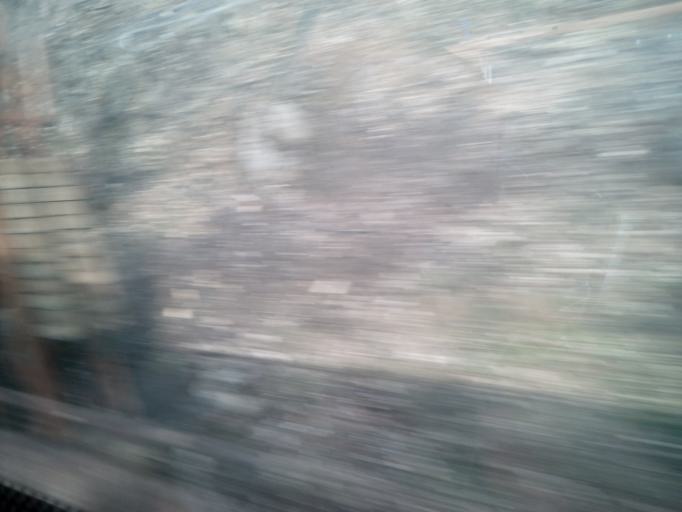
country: SK
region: Zilinsky
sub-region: Okres Liptovsky Mikulas
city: Hybe
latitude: 49.0582
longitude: 19.9539
